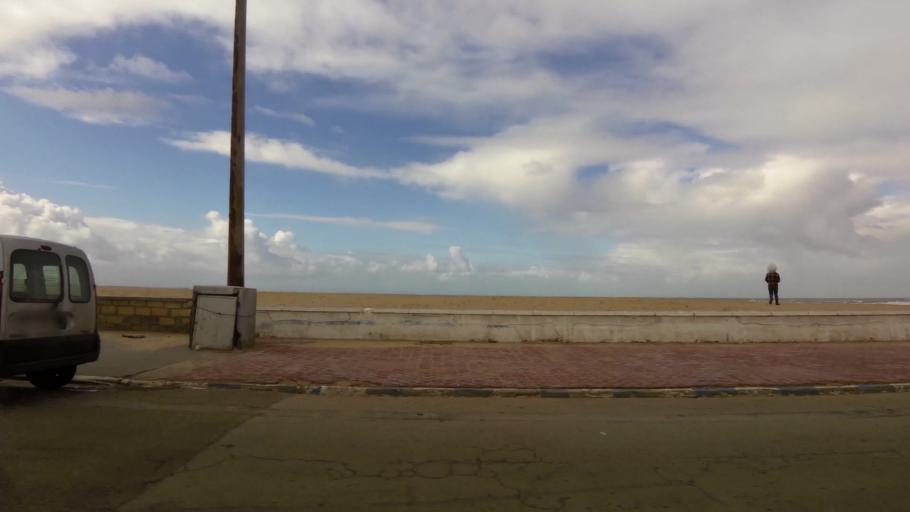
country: MA
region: Doukkala-Abda
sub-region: El-Jadida
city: El Jadida
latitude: 33.2442
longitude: -8.4869
